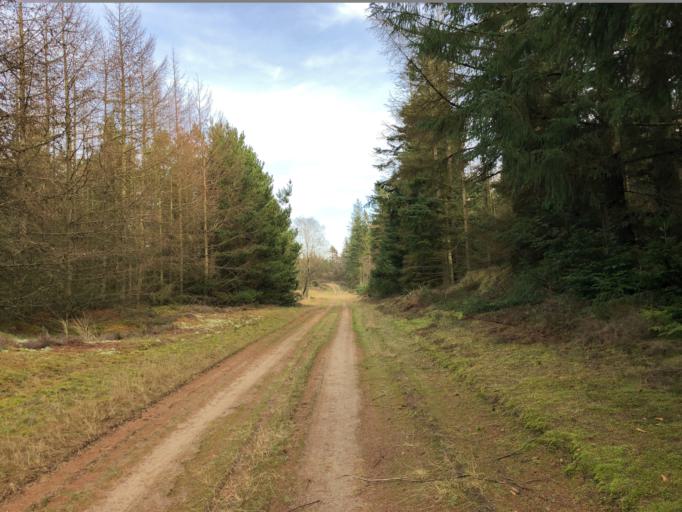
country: DK
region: Central Jutland
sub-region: Holstebro Kommune
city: Ulfborg
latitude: 56.2613
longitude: 8.3784
